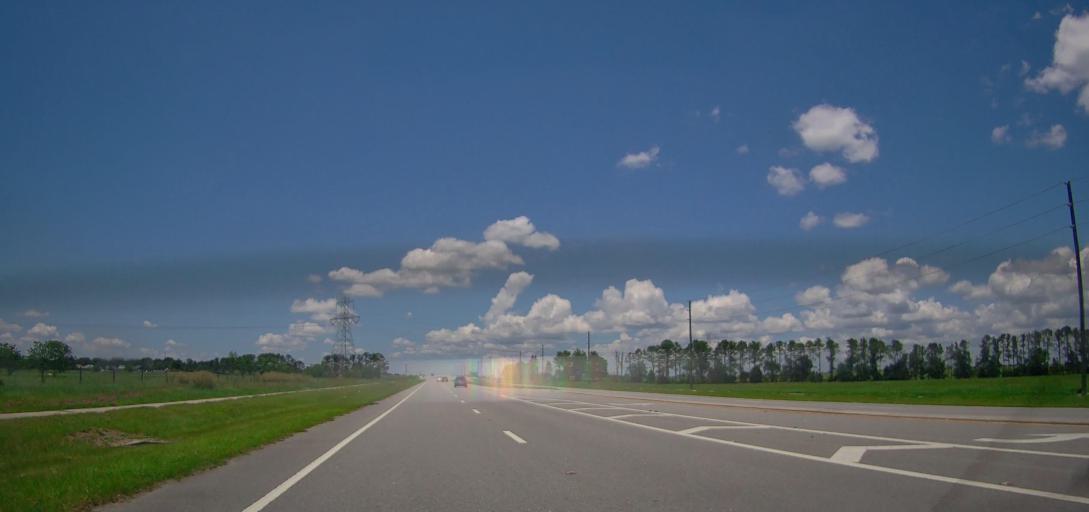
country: US
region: Florida
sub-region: Marion County
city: Silver Springs Shores
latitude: 29.0674
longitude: -82.0217
